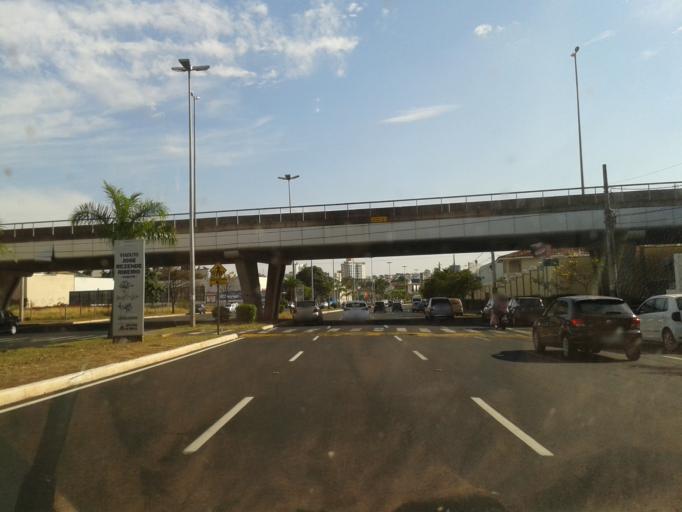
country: BR
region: Minas Gerais
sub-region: Uberlandia
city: Uberlandia
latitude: -18.9296
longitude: -48.2775
